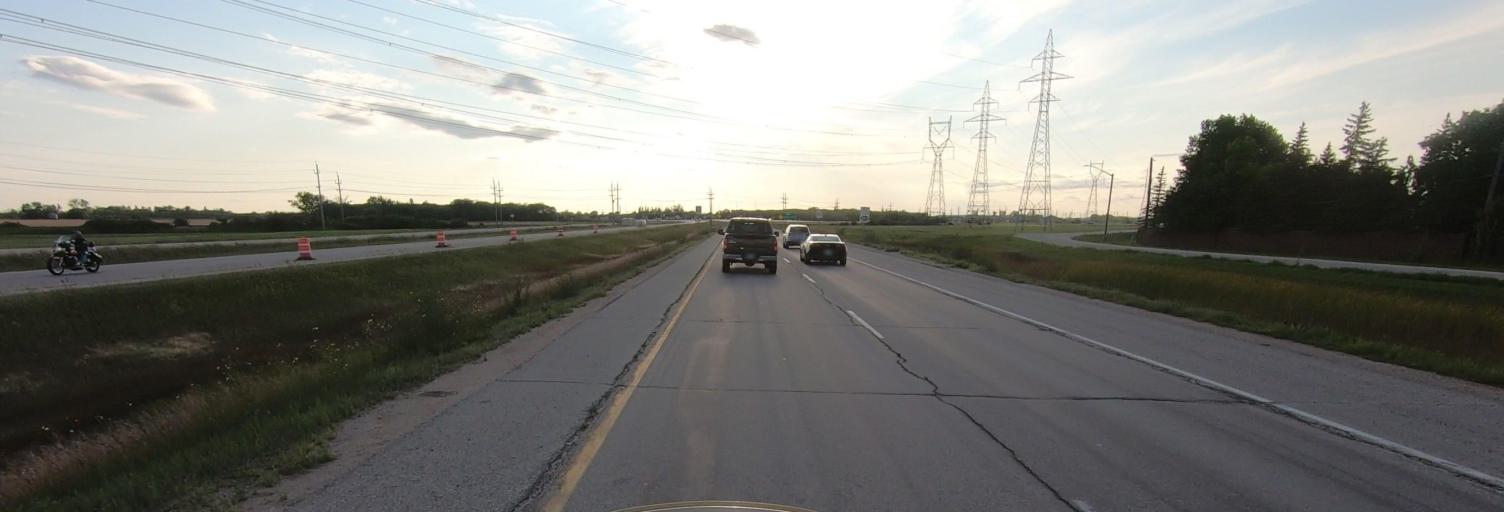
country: CA
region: Manitoba
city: Winnipeg
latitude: 49.9671
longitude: -97.0023
